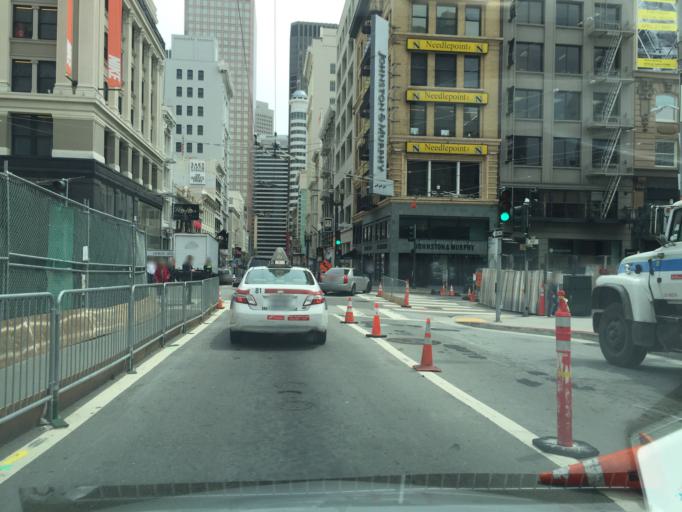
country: US
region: California
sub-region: San Francisco County
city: San Francisco
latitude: 37.7884
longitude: -122.4072
